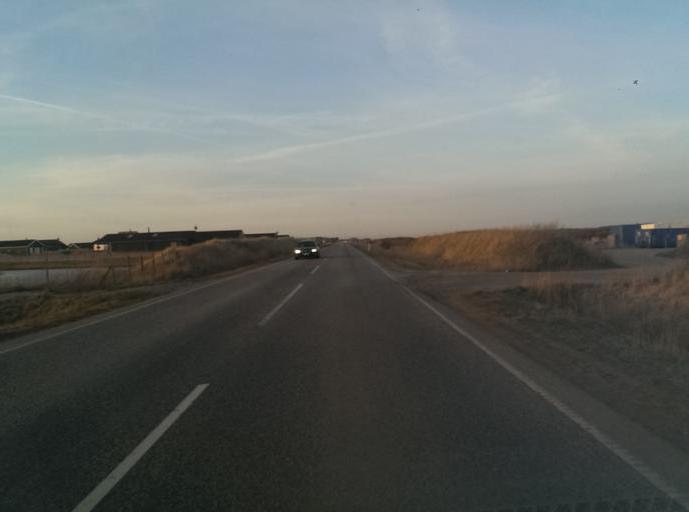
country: DK
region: Central Jutland
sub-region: Ringkobing-Skjern Kommune
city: Hvide Sande
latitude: 56.1244
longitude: 8.1168
